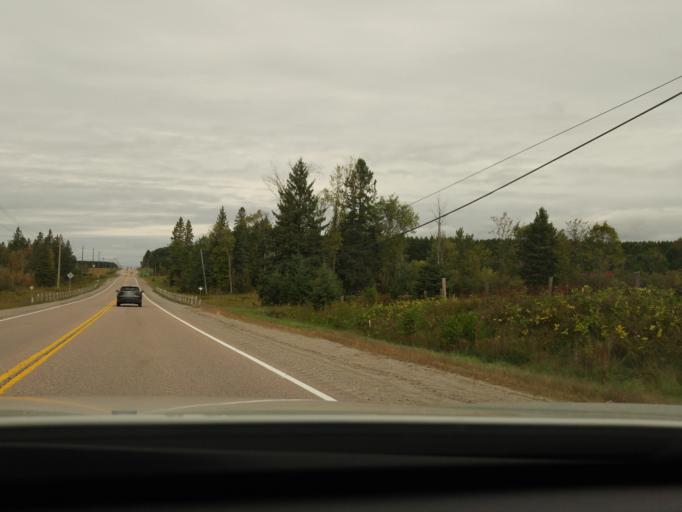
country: CA
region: Ontario
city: Renfrew
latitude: 45.5859
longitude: -76.8304
